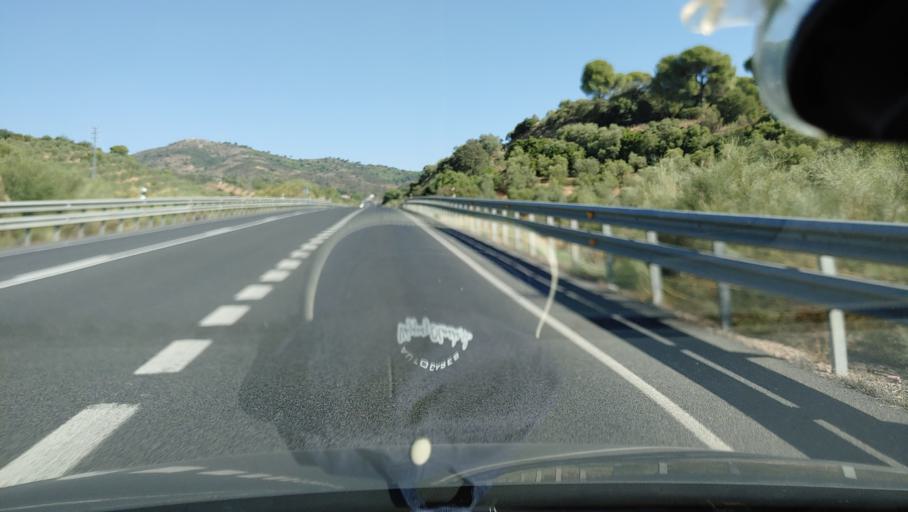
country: ES
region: Andalusia
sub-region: Province of Cordoba
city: Cordoba
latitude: 37.9619
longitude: -4.7671
